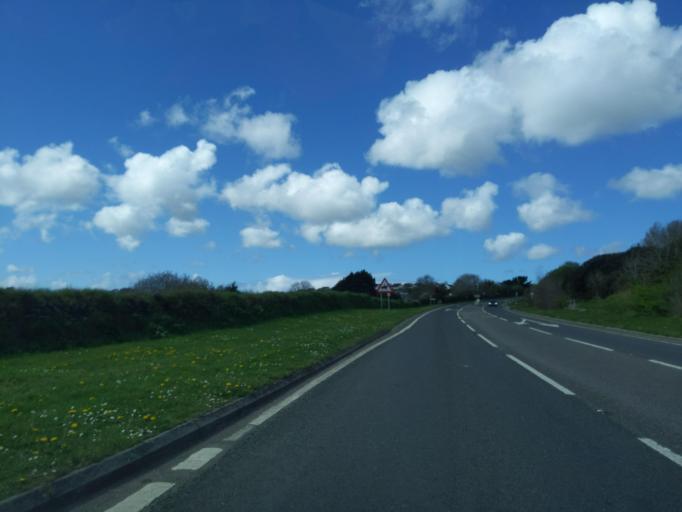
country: GB
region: England
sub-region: Cornwall
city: Wadebridge
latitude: 50.5121
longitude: -4.8168
